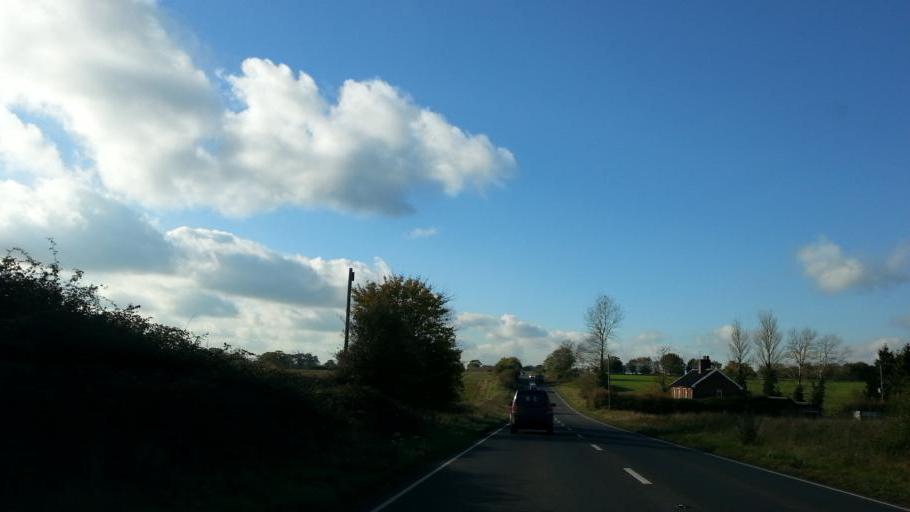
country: GB
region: England
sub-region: Norfolk
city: Diss
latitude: 52.3647
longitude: 1.2046
